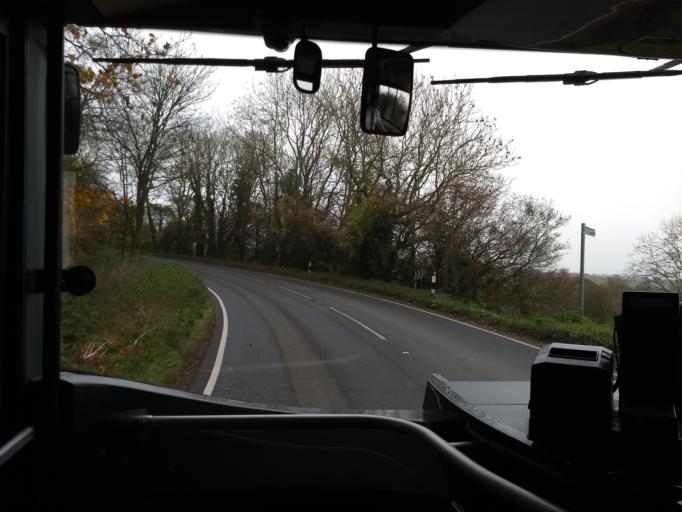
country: GB
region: England
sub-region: Isle of Wight
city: Newchurch
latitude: 50.6818
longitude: -1.2477
